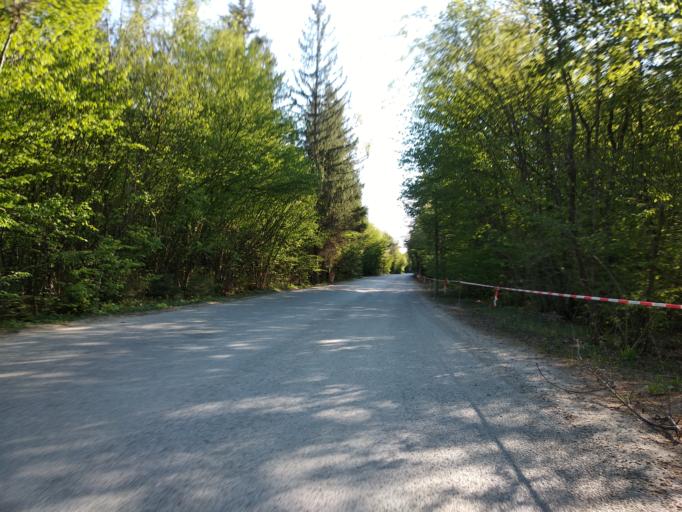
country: DE
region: Bavaria
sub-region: Upper Bavaria
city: Grasbrunn
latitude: 48.0711
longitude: 11.7346
